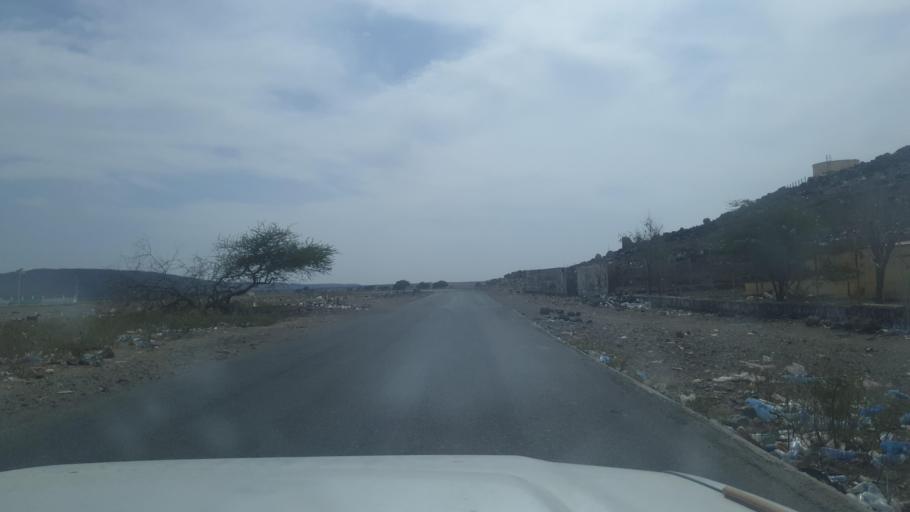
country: DJ
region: Dikhil
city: Dikhil
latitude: 11.1627
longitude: 42.5039
